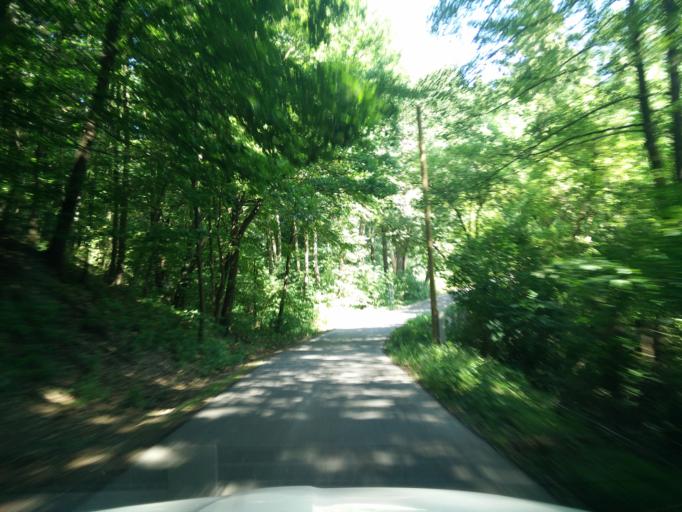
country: SK
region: Nitriansky
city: Prievidza
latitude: 48.7475
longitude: 18.6334
